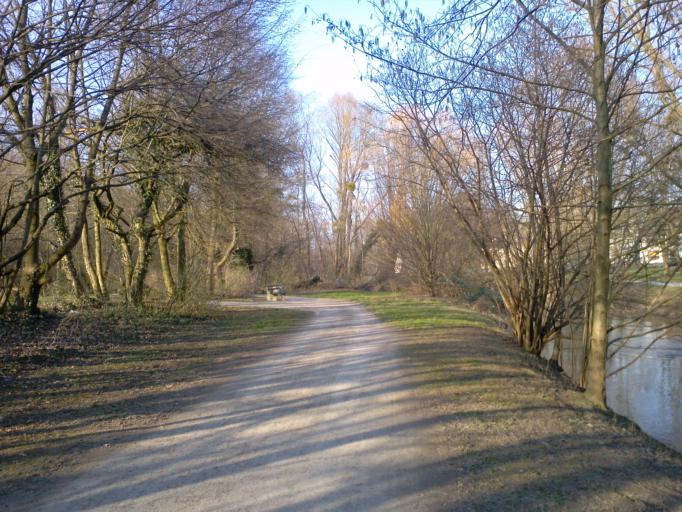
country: DE
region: Baden-Wuerttemberg
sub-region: Karlsruhe Region
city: Karlsruhe
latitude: 48.9862
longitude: 8.3962
